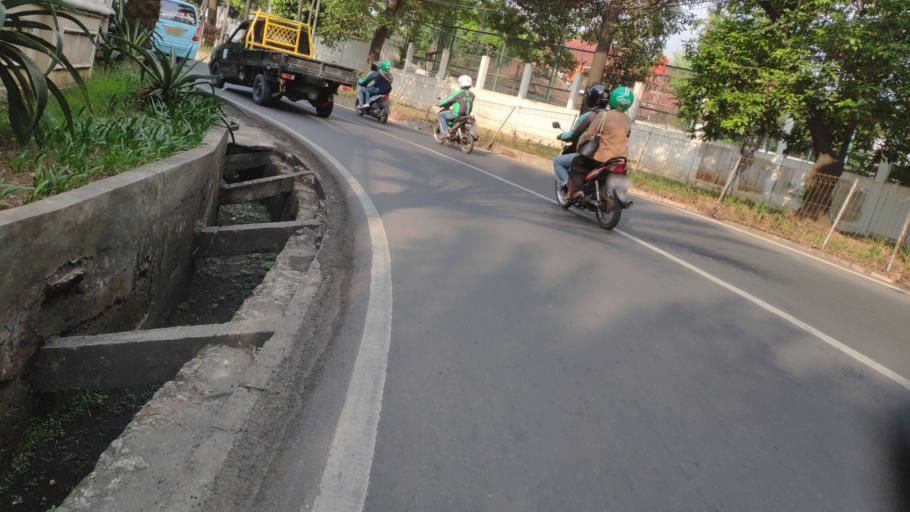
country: ID
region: West Java
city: Pamulang
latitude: -6.3149
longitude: 106.8124
